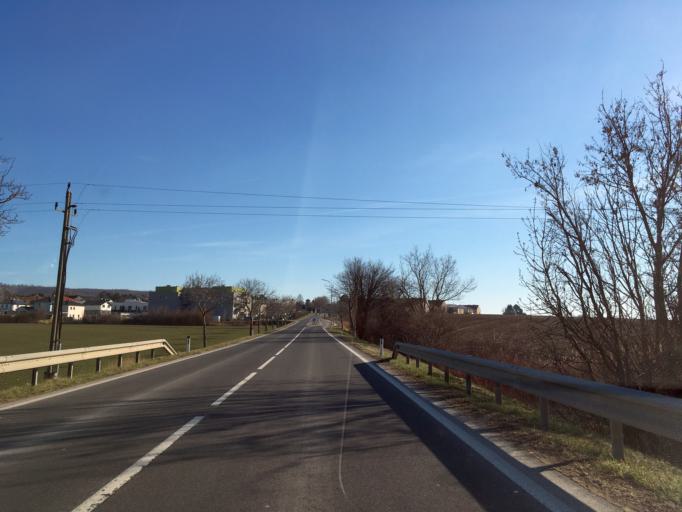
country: AT
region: Burgenland
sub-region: Eisenstadt-Umgebung
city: Hornstein
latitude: 47.8902
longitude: 16.4383
